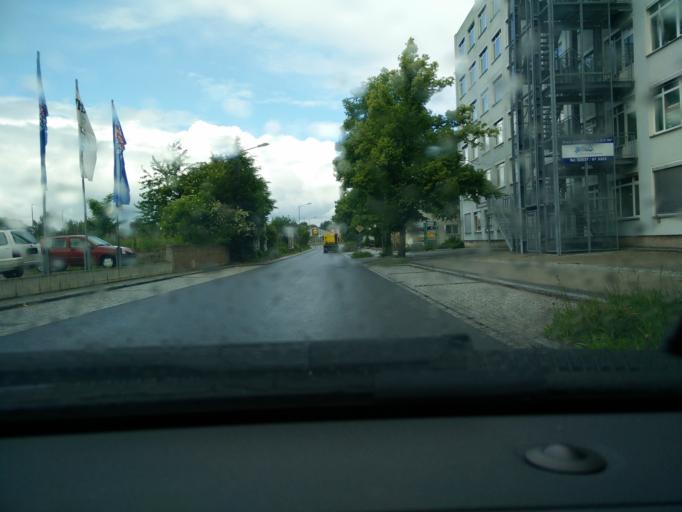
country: DE
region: Saxony
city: Grimma
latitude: 51.2266
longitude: 12.7154
